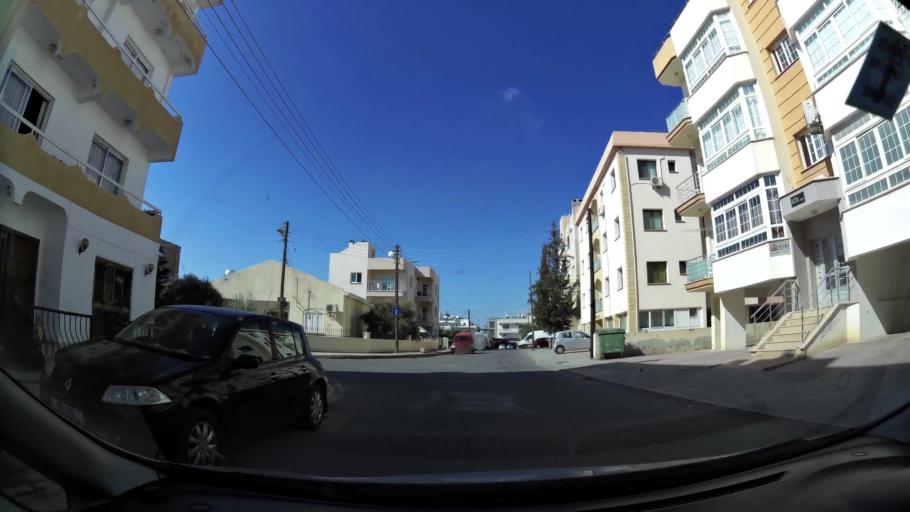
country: CY
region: Lefkosia
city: Nicosia
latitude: 35.2088
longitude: 33.3364
